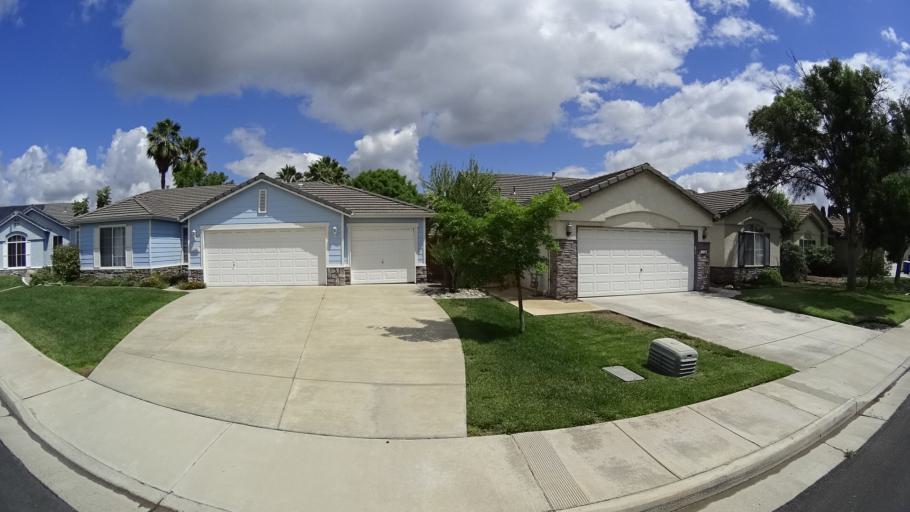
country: US
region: California
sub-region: Kings County
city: Lucerne
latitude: 36.3601
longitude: -119.6630
